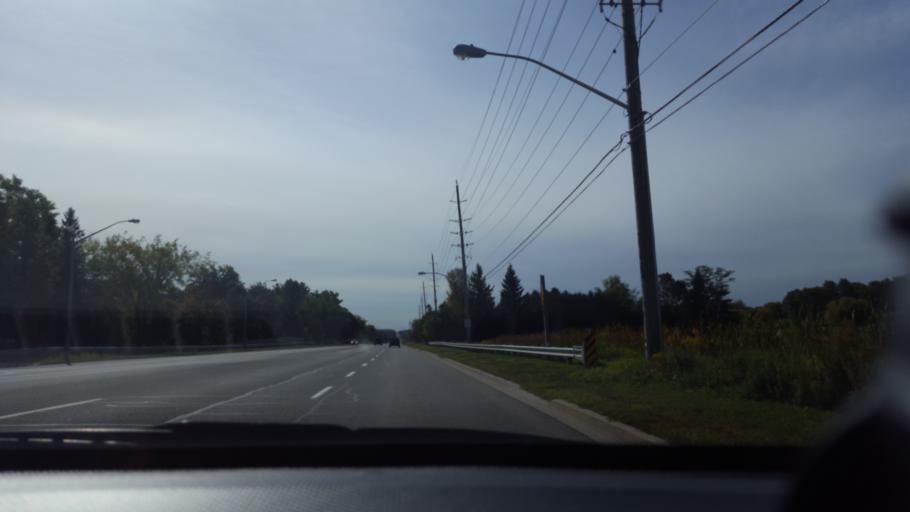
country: CA
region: Ontario
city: Newmarket
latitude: 44.0067
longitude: -79.4972
